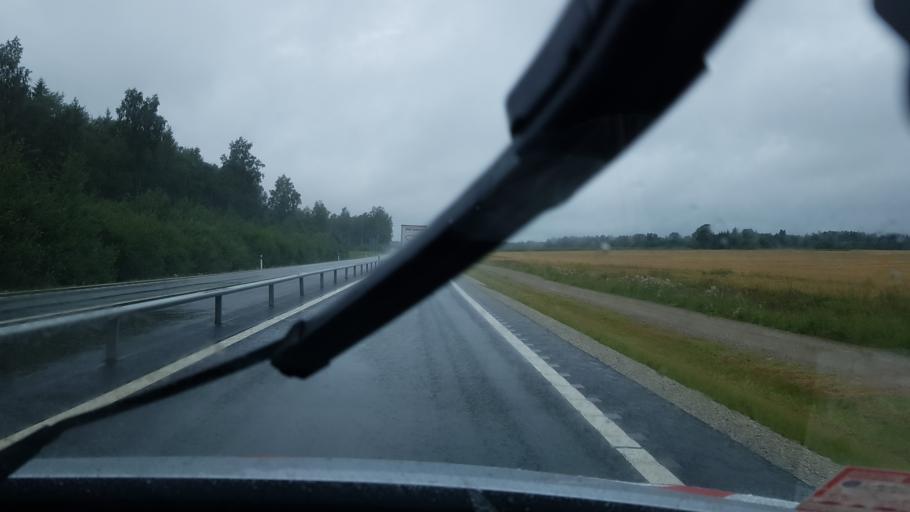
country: EE
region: Jogevamaa
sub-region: Jogeva linn
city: Jogeva
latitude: 58.5946
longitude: 26.2450
